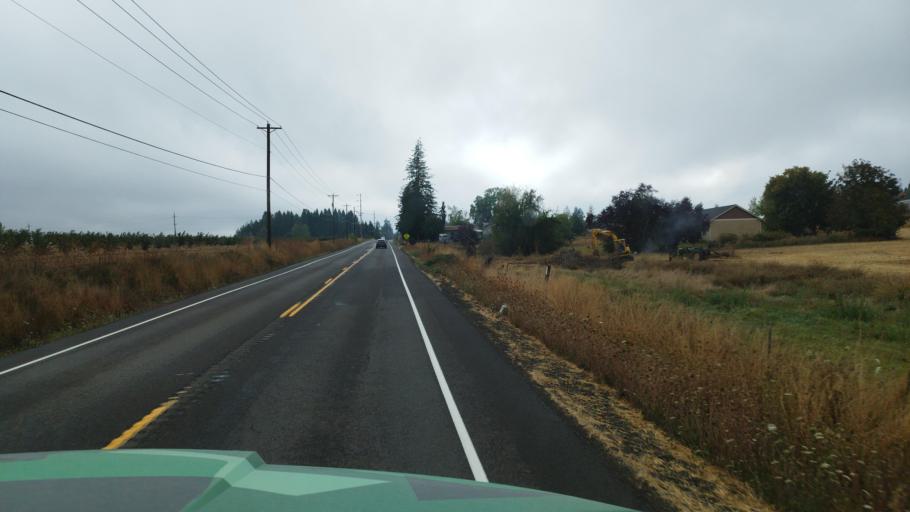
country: US
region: Oregon
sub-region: Yamhill County
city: Yamhill
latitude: 45.3237
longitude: -123.1789
